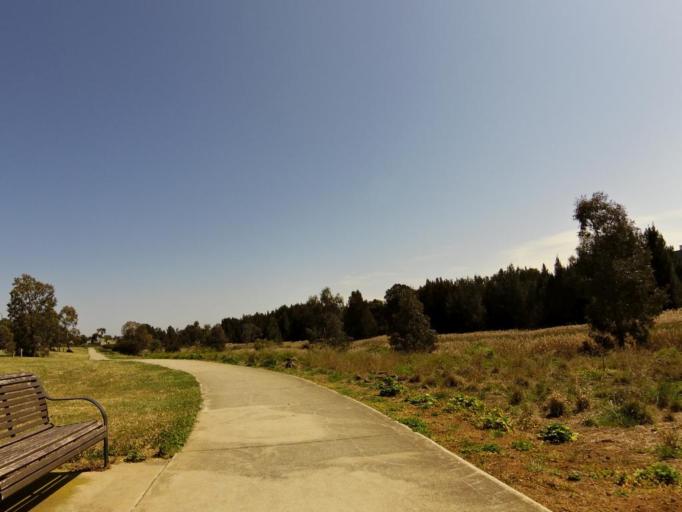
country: AU
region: Victoria
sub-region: Wyndham
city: Williams Landing
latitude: -37.8743
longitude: 144.7444
